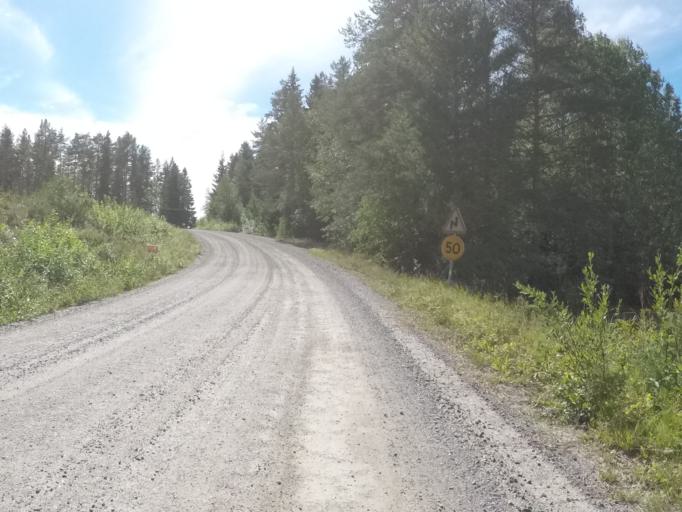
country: SE
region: Vaesterbotten
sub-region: Robertsfors Kommun
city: Robertsfors
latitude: 64.0034
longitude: 20.8121
